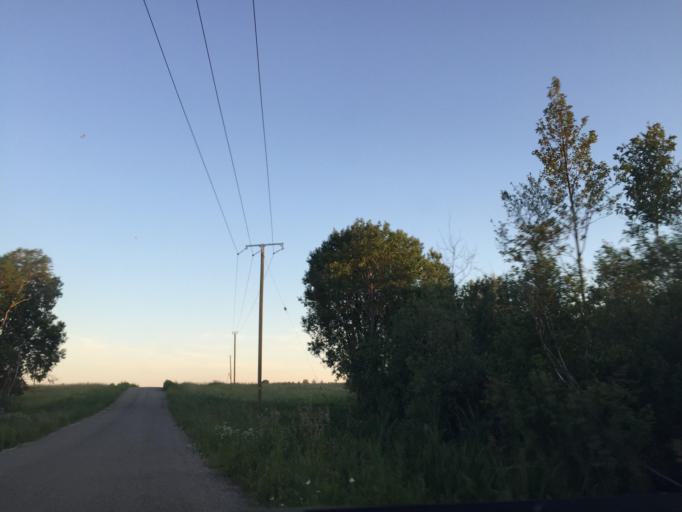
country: LV
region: Rezekne
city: Rezekne
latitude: 56.3721
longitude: 27.4090
